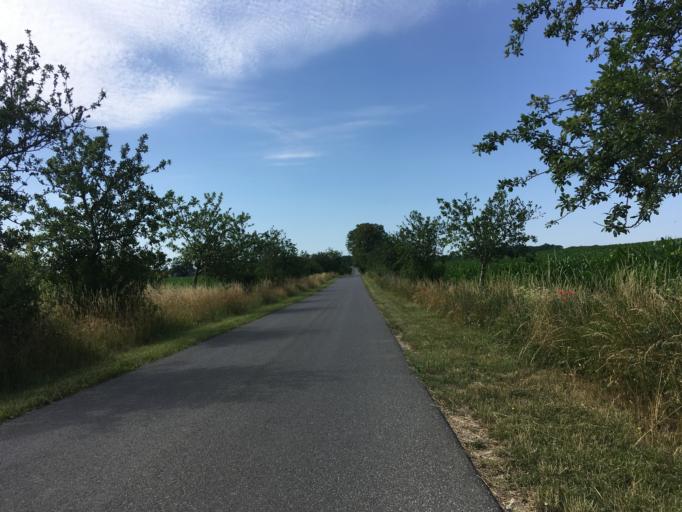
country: DE
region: Brandenburg
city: Zichow
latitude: 53.2016
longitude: 14.0437
